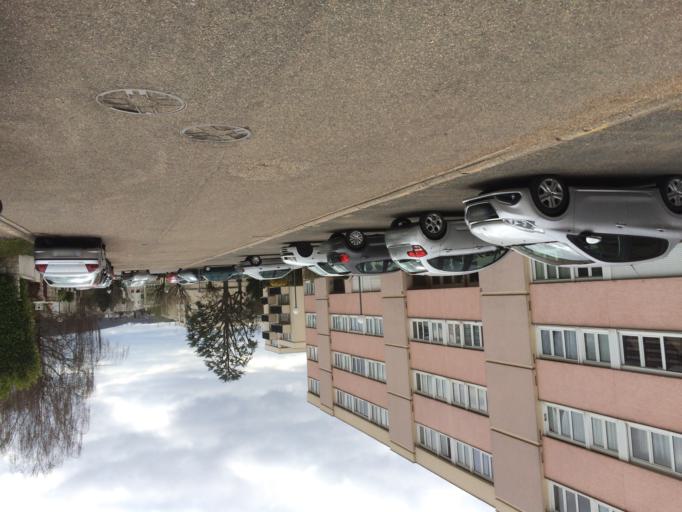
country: FR
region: Ile-de-France
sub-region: Departement de l'Essonne
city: Palaiseau
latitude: 48.7131
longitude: 2.2496
